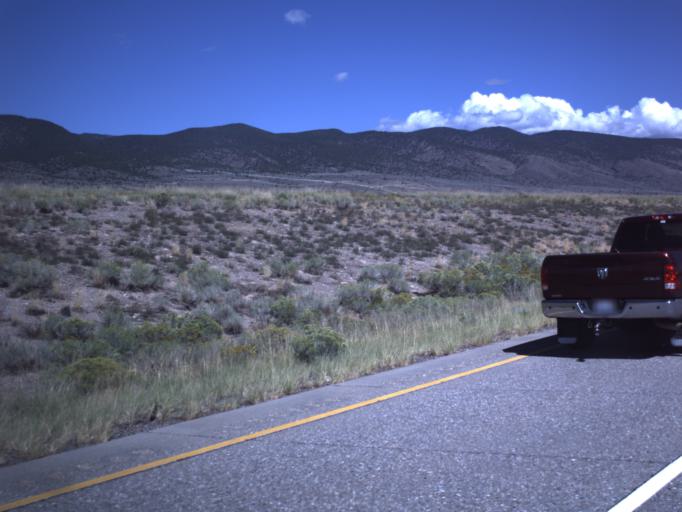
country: US
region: Utah
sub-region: Sevier County
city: Monroe
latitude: 38.6201
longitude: -112.2279
